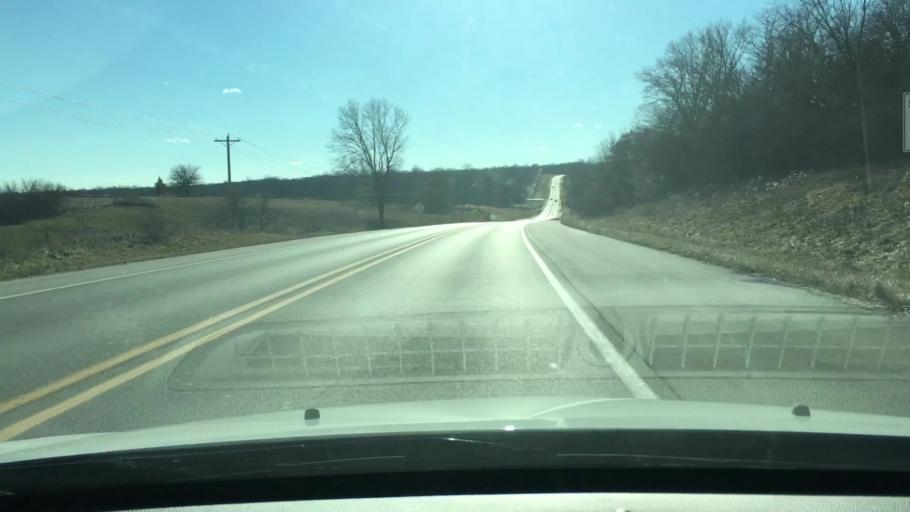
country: US
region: Illinois
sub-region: Pike County
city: Griggsville
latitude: 39.6700
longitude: -90.7697
